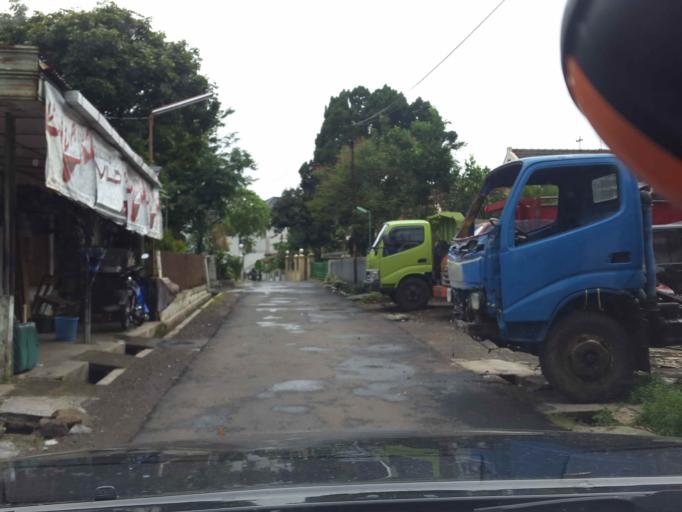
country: ID
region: Central Java
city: Salatiga
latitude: -7.3401
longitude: 110.5075
